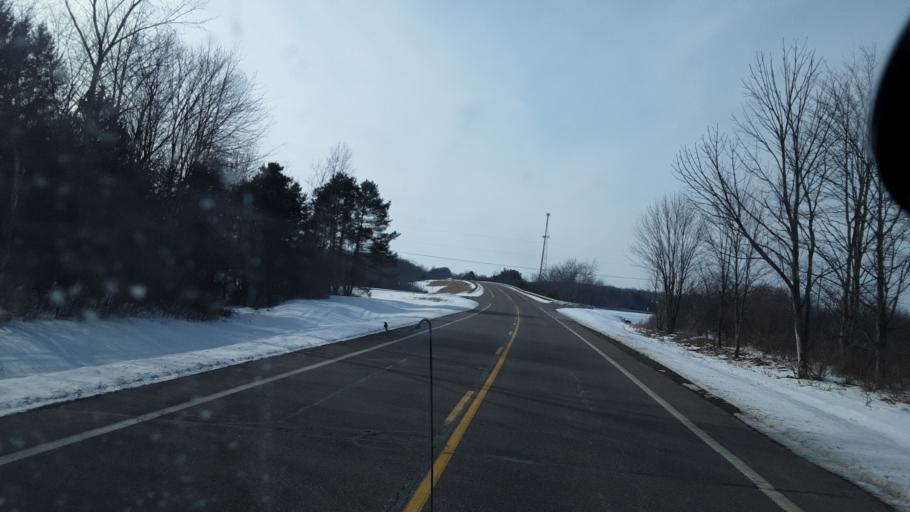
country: US
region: Ohio
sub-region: Stark County
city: Alliance
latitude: 41.0327
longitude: -81.1627
